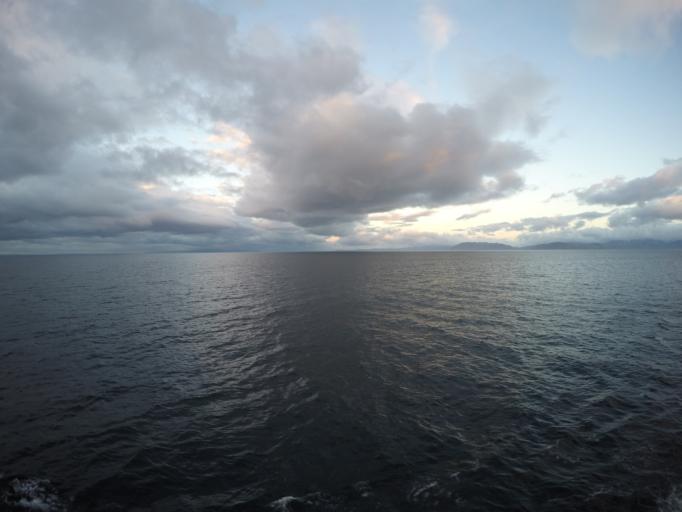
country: IS
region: West
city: Olafsvik
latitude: 65.1110
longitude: -23.3787
